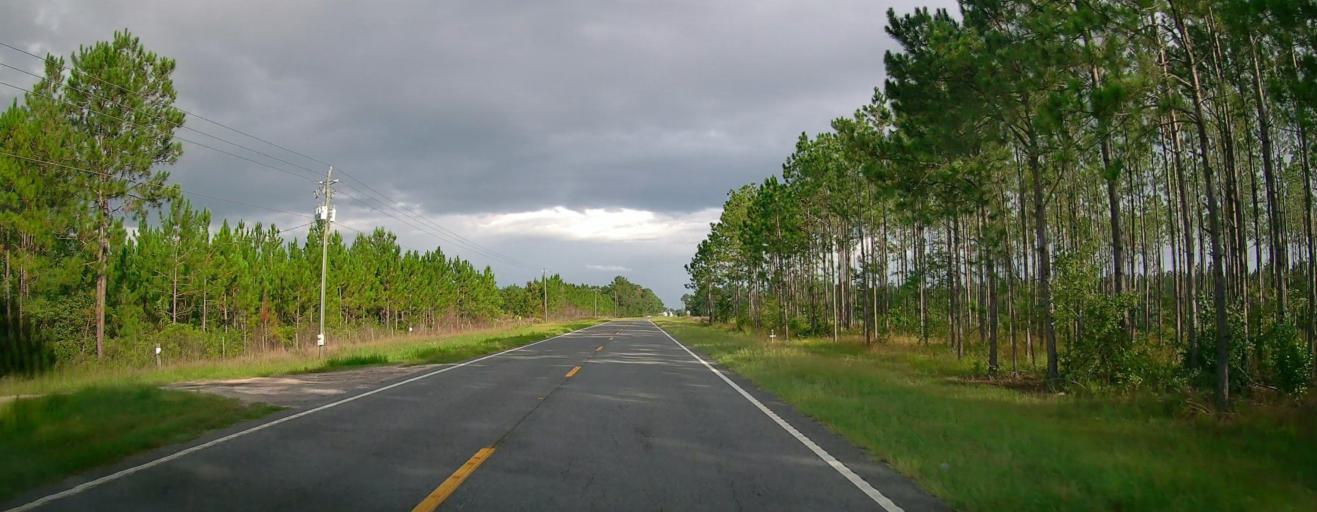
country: US
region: Georgia
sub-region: Coffee County
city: Nicholls
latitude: 31.3598
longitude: -82.6228
